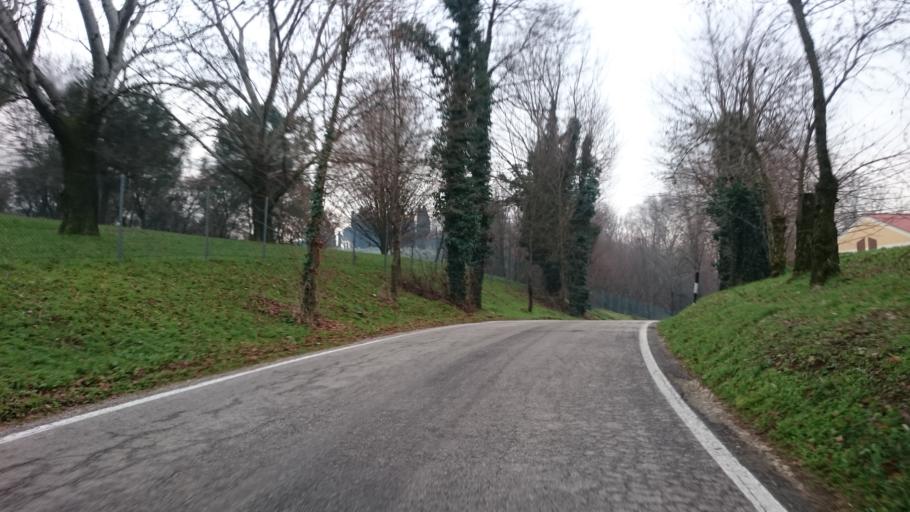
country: IT
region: Veneto
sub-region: Provincia di Vicenza
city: Montegalda
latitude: 45.4546
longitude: 11.6680
